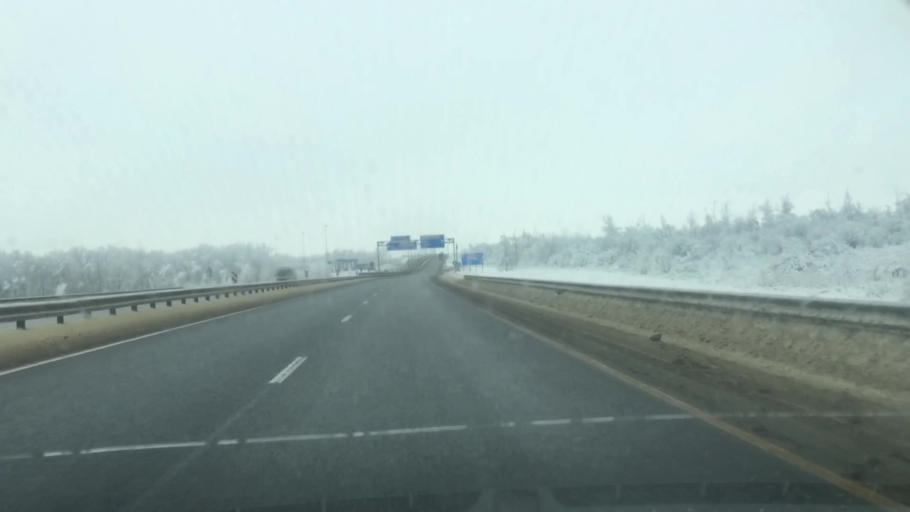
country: RU
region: Lipetsk
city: Yelets
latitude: 52.5554
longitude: 38.7155
